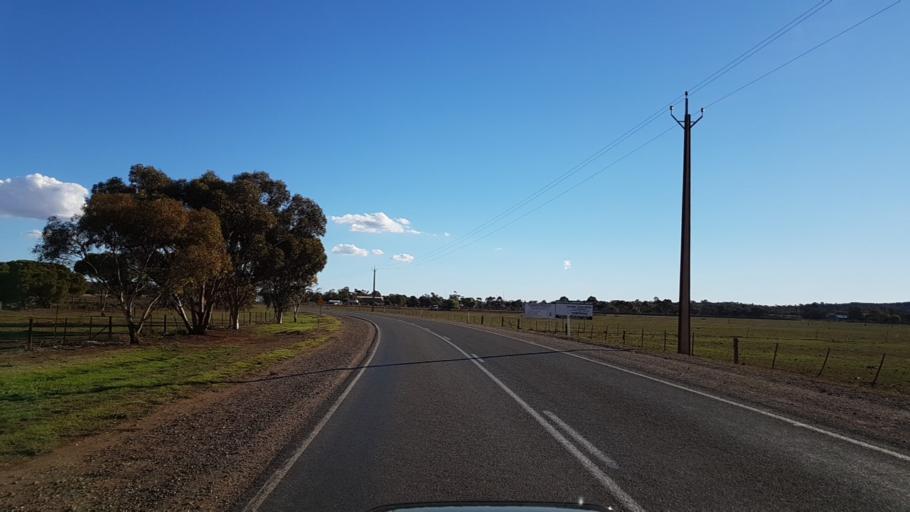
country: AU
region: South Australia
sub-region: Peterborough
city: Peterborough
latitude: -32.9704
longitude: 138.8527
